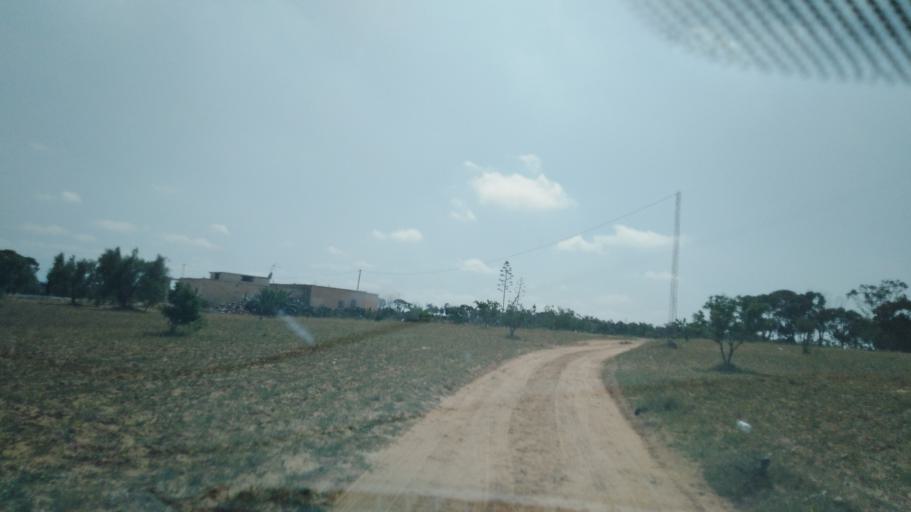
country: TN
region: Safaqis
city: Sfax
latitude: 34.7265
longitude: 10.5716
